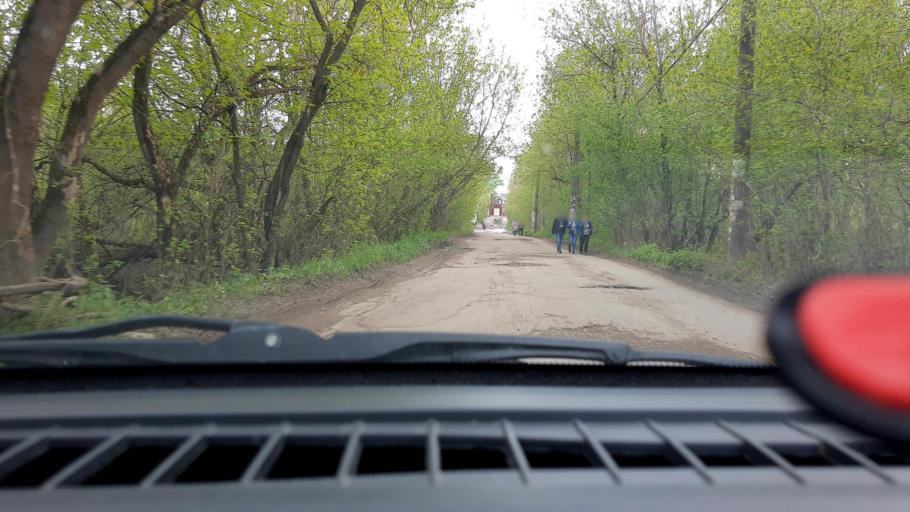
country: RU
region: Nizjnij Novgorod
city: Neklyudovo
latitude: 56.3829
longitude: 43.8353
